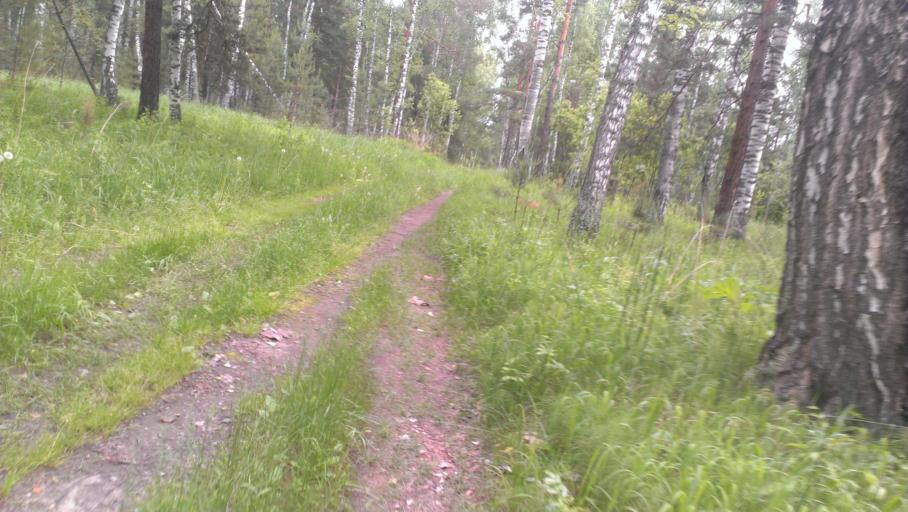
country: RU
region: Altai Krai
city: Sannikovo
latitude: 53.3457
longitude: 84.0419
